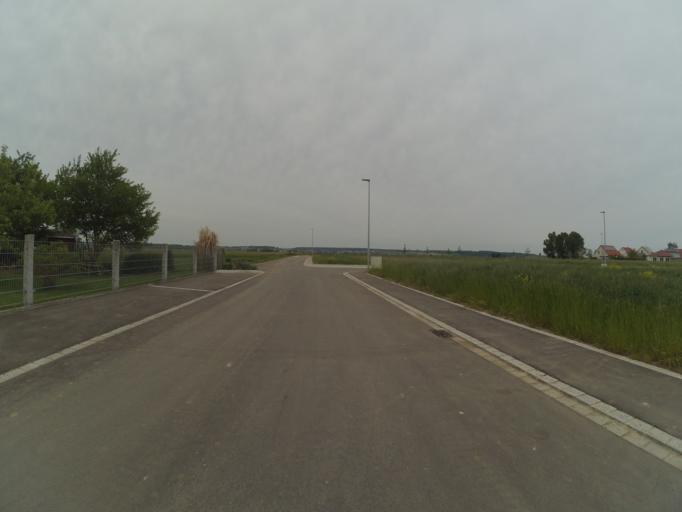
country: DE
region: Baden-Wuerttemberg
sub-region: Regierungsbezirk Stuttgart
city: Niederstotzingen
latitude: 48.5108
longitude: 10.2553
